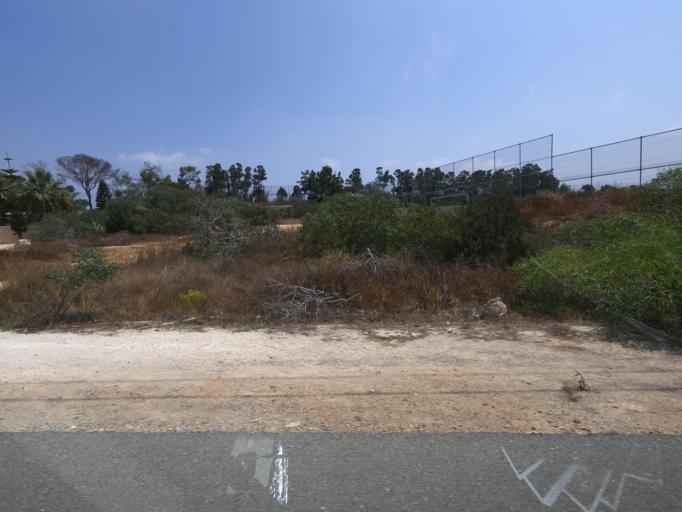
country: CY
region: Ammochostos
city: Ayia Napa
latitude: 34.9918
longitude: 34.0119
